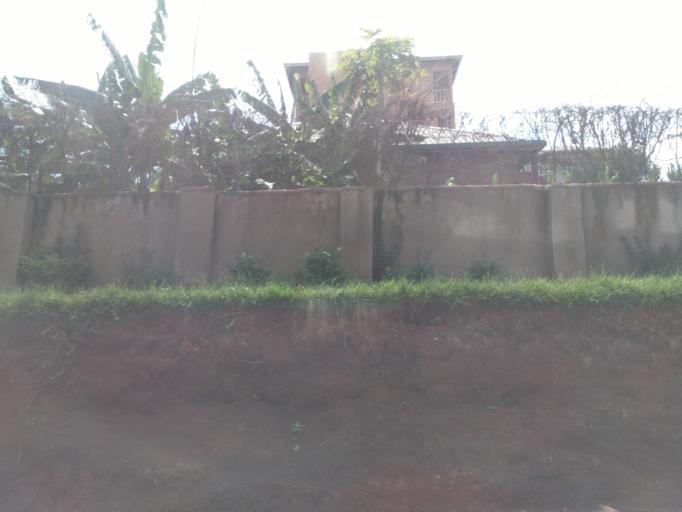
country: UG
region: Central Region
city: Kampala Central Division
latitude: 0.3427
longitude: 32.5674
